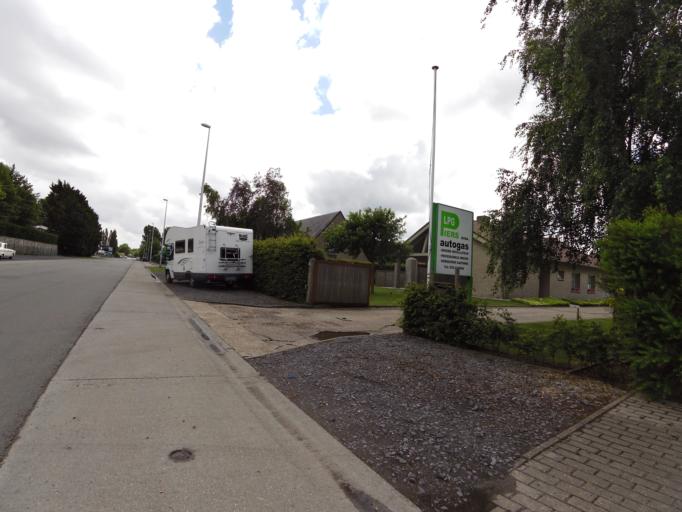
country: BE
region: Flanders
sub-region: Provincie West-Vlaanderen
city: Gistel
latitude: 51.1496
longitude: 2.9449
